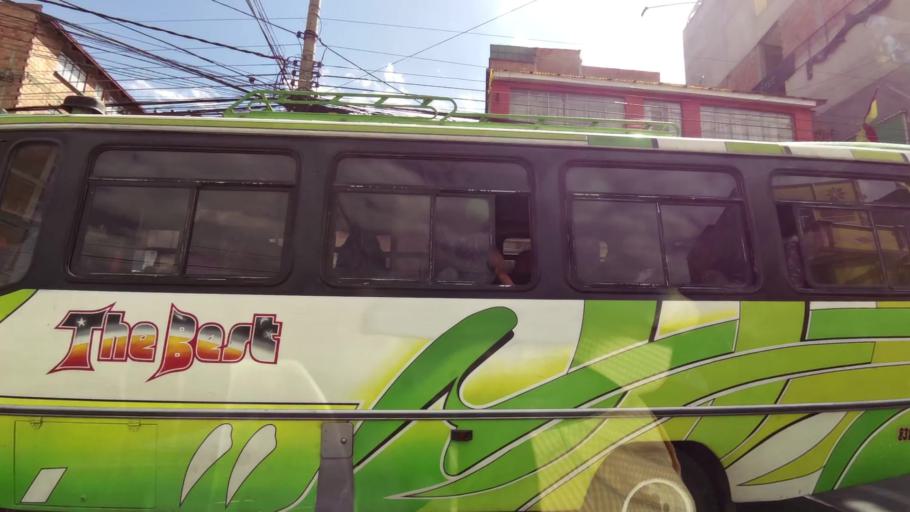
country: BO
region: La Paz
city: La Paz
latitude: -16.4819
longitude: -68.1220
